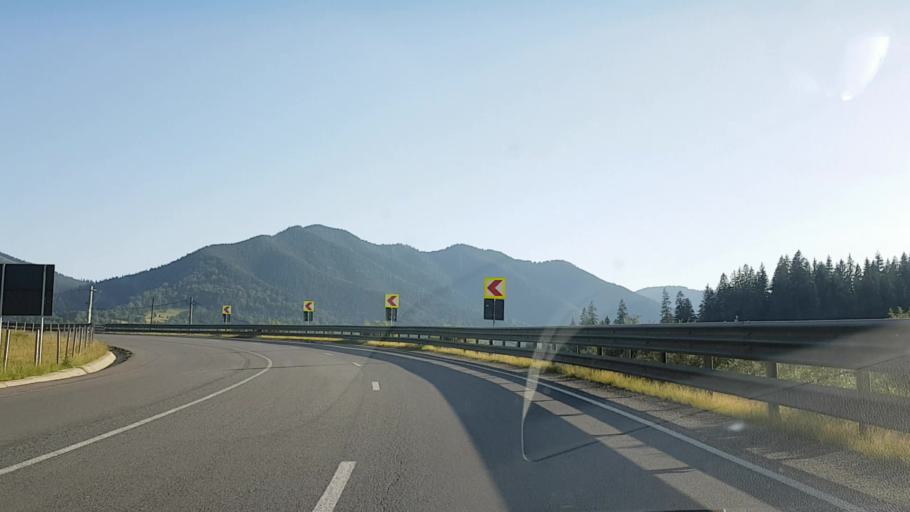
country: RO
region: Bistrita-Nasaud
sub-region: Comuna Lunca Ilvei
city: Lunca Ilvei
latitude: 47.2311
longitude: 24.9669
